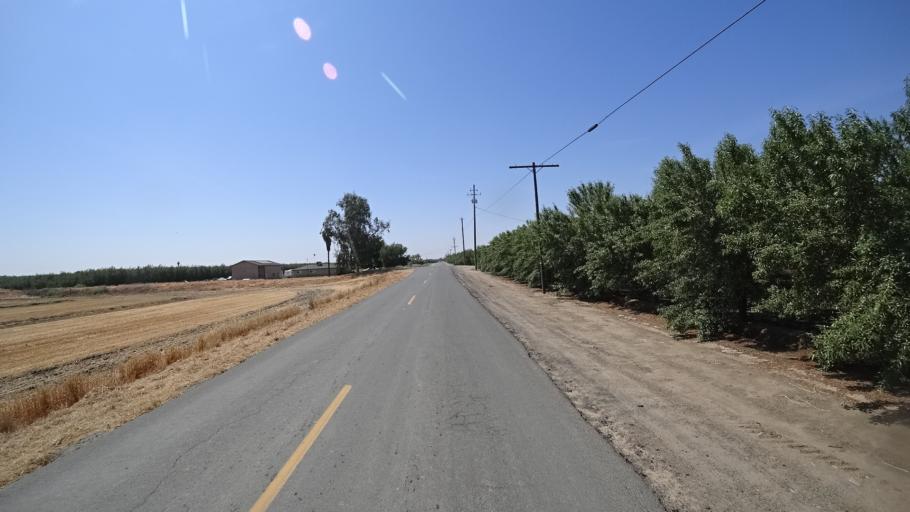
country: US
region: California
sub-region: Fresno County
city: Riverdale
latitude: 36.3992
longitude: -119.8693
